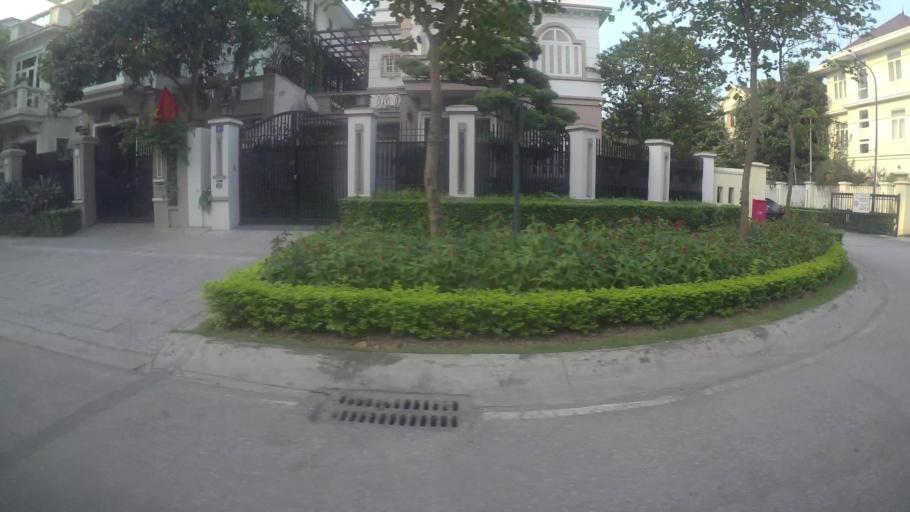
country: VN
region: Ha Noi
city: Tay Ho
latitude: 21.0743
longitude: 105.8024
